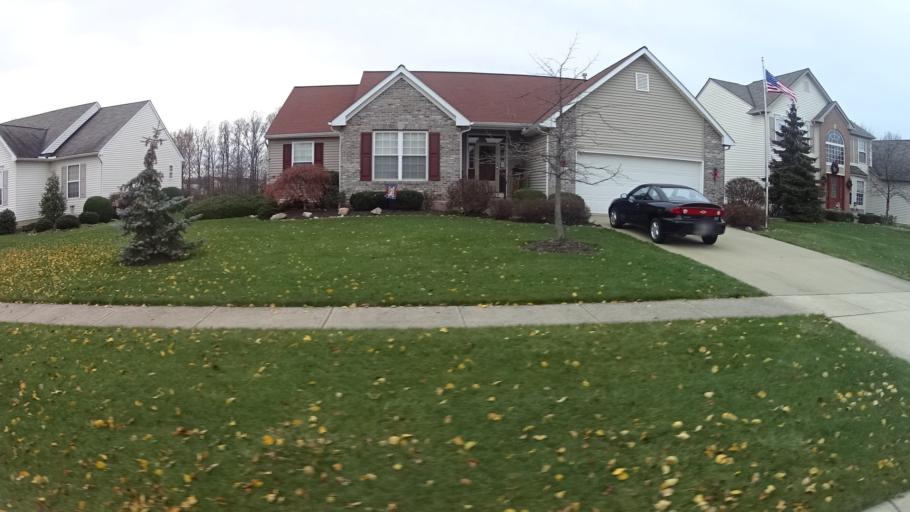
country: US
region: Ohio
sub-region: Lorain County
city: Sheffield
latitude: 41.4137
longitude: -82.0552
